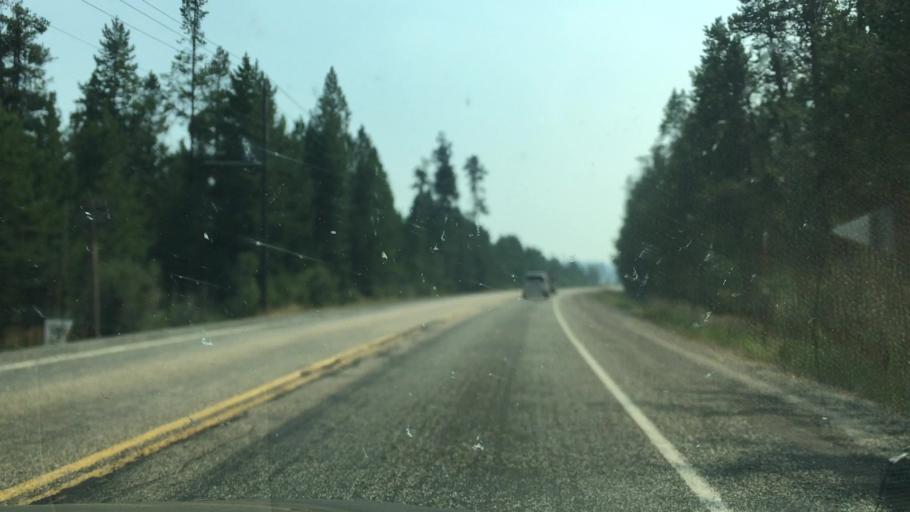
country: US
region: Idaho
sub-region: Valley County
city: Cascade
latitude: 44.4024
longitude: -116.0010
